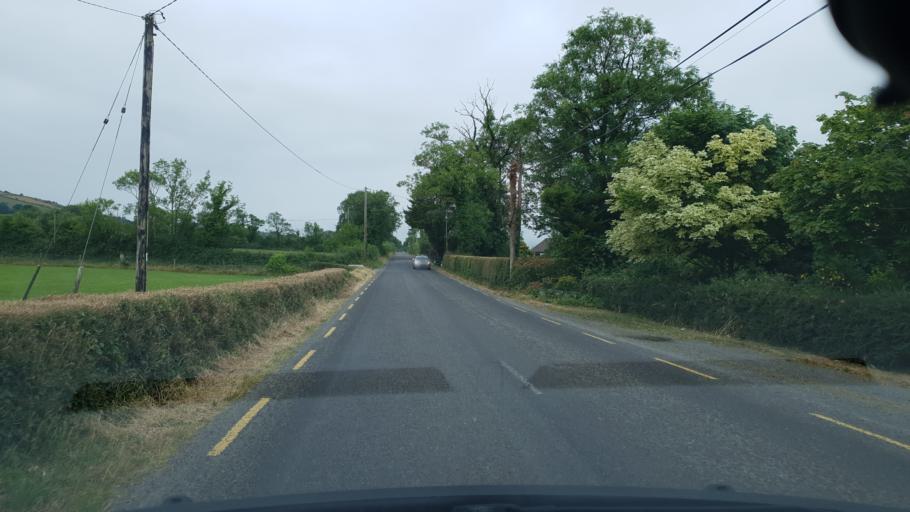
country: IE
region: Munster
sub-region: Ciarrai
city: Tralee
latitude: 52.1631
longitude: -9.6410
